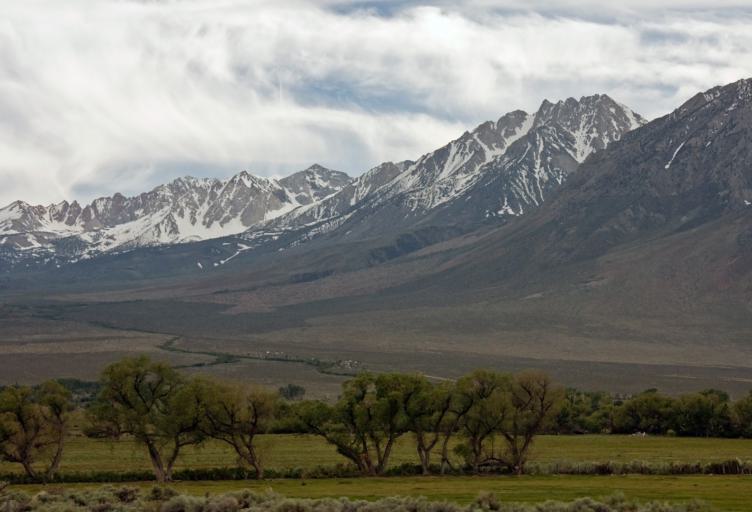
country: US
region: California
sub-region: Inyo County
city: West Bishop
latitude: 37.4080
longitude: -118.5479
